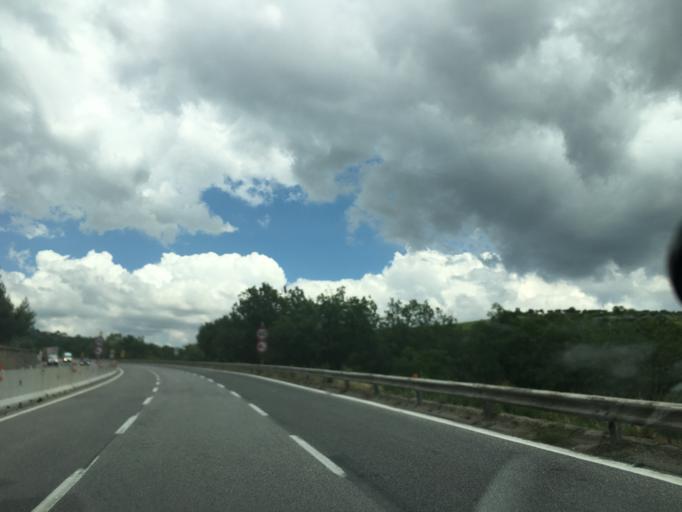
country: IT
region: Campania
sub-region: Provincia di Avellino
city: Mirabella Eclano
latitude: 41.0710
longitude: 14.9735
